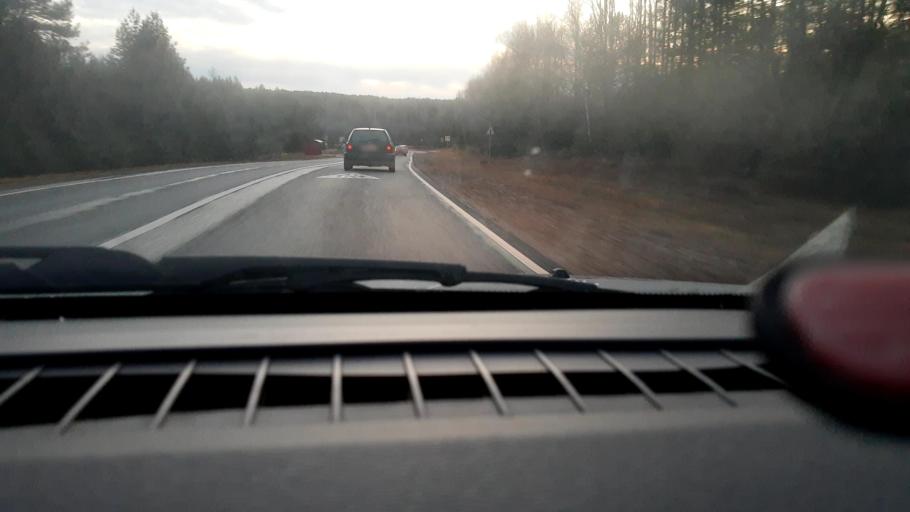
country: RU
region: Nizjnij Novgorod
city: Krasnyye Baki
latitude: 57.0316
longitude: 45.1194
